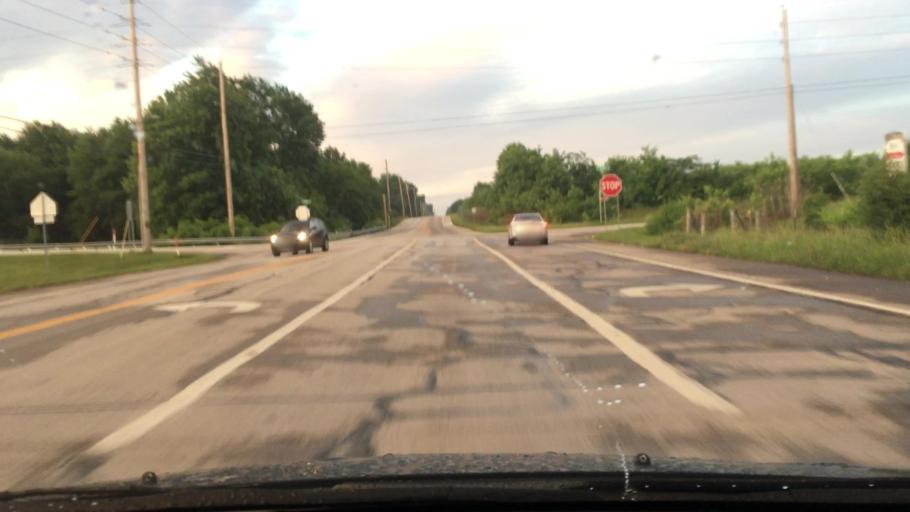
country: US
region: Missouri
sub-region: Jackson County
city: Lees Summit
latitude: 38.8689
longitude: -94.4163
